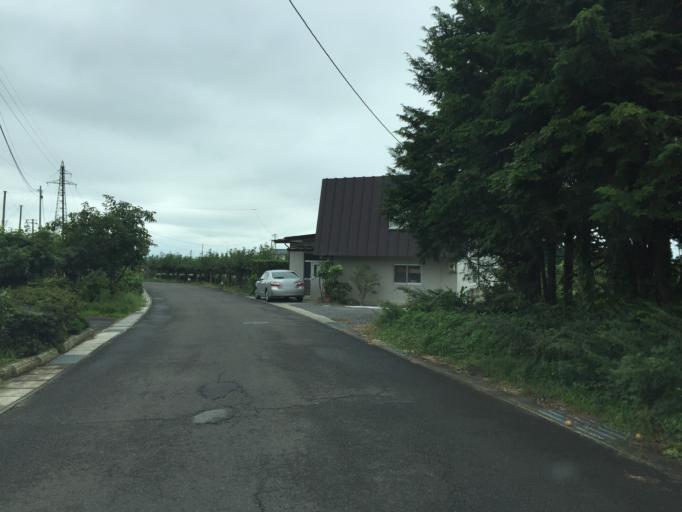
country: JP
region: Fukushima
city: Fukushima-shi
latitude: 37.7684
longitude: 140.3987
